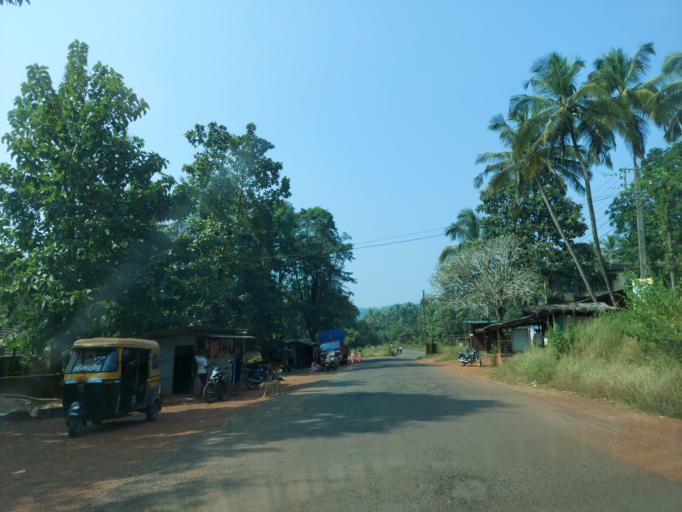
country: IN
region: Maharashtra
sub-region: Sindhudurg
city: Kudal
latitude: 15.9696
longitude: 73.6387
